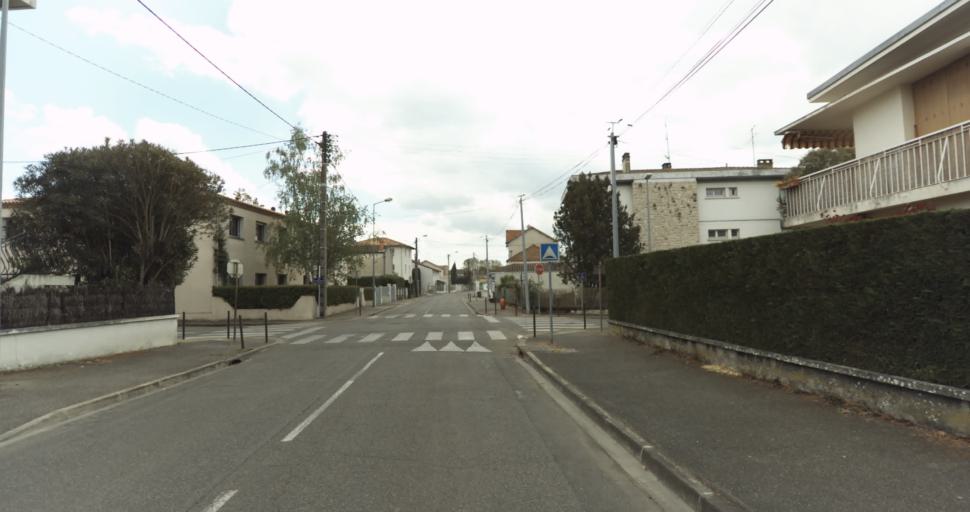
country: FR
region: Aquitaine
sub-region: Departement du Lot-et-Garonne
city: Agen
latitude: 44.1973
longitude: 0.6225
